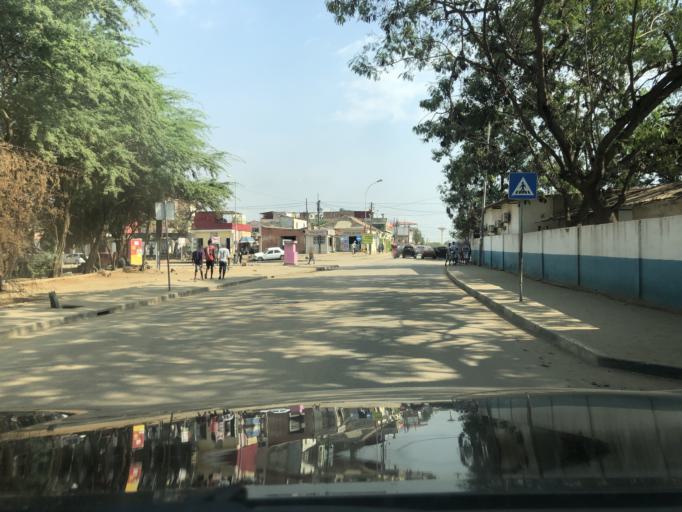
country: AO
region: Luanda
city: Luanda
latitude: -8.8477
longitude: 13.2596
